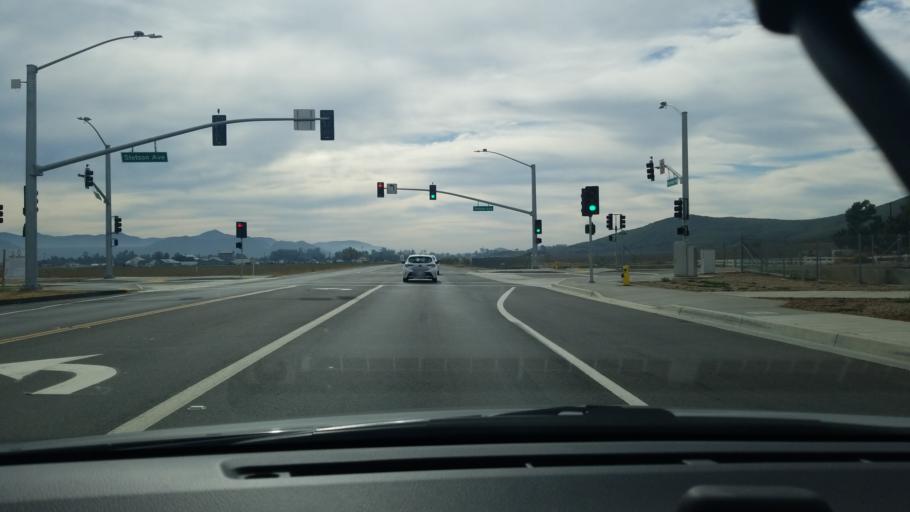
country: US
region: California
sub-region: Riverside County
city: Green Acres
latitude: 33.7296
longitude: -117.0765
